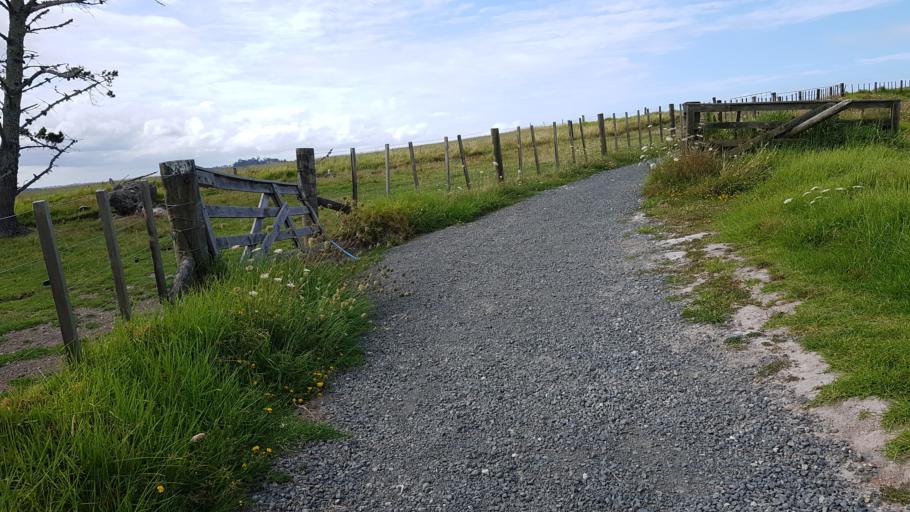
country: NZ
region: Auckland
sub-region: Auckland
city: Rothesay Bay
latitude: -36.6658
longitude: 174.7457
